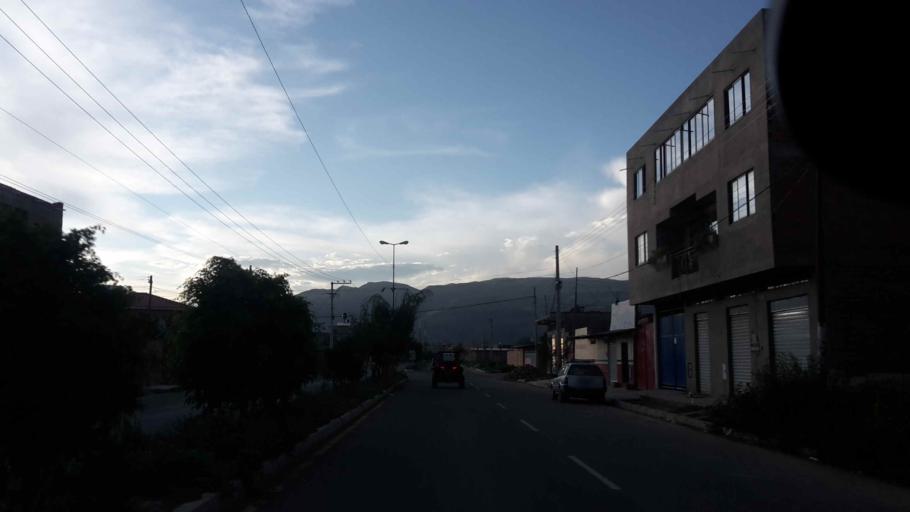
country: BO
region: Cochabamba
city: Punata
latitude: -17.5409
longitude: -65.8316
